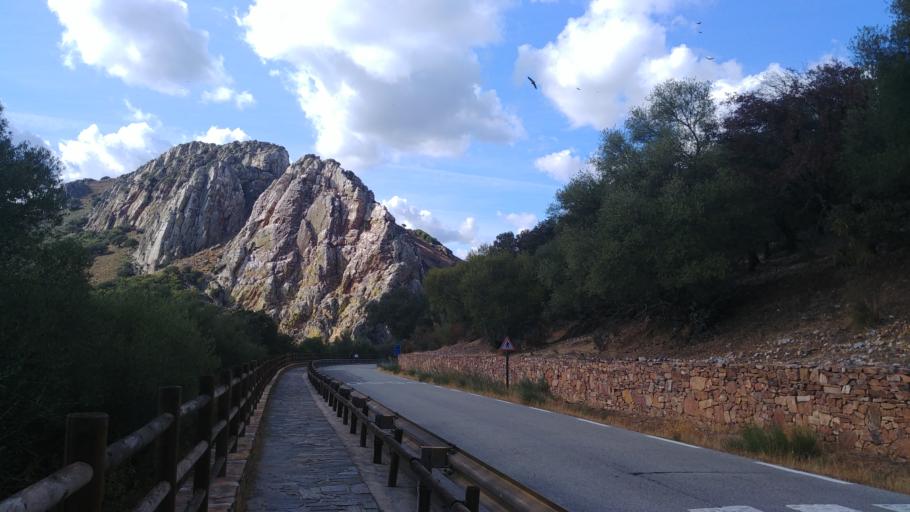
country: ES
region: Extremadura
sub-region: Provincia de Caceres
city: Torrejon el Rubio
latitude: 39.8256
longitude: -6.0557
